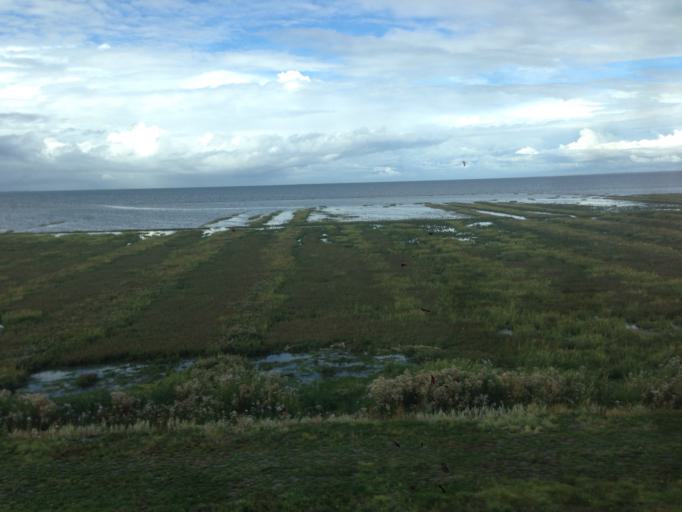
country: DE
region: Schleswig-Holstein
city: Friedrich-Wilhelm-Lubke-Koog
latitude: 54.8849
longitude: 8.5619
